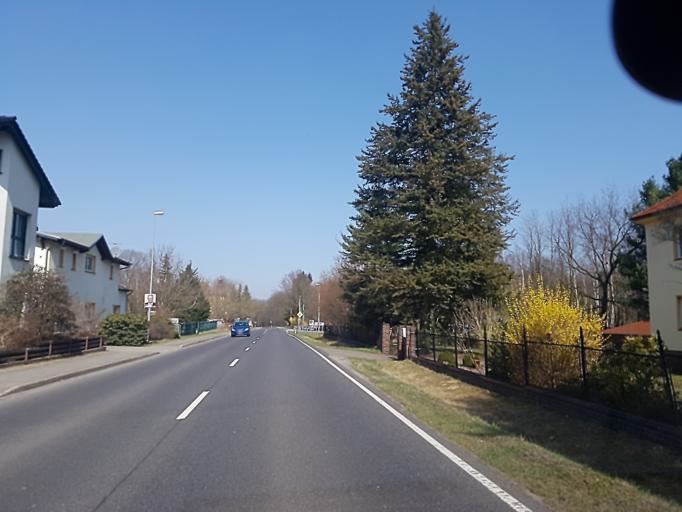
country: DE
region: Brandenburg
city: Tschernitz
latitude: 51.6397
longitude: 14.5827
